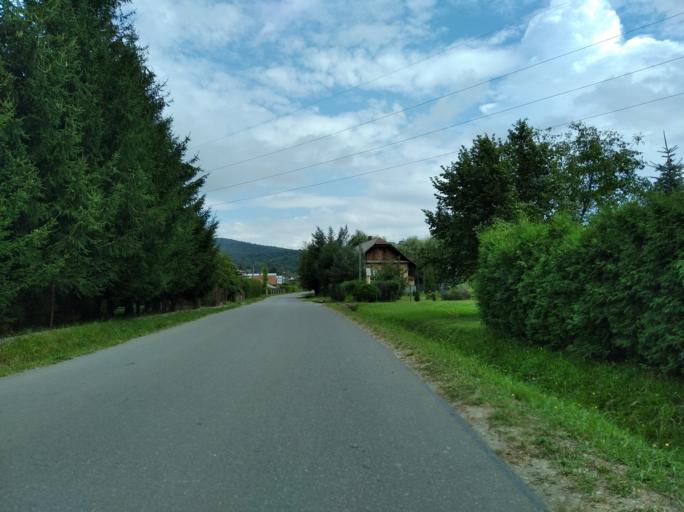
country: PL
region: Subcarpathian Voivodeship
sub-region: Powiat krosnienski
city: Odrzykon
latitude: 49.7413
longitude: 21.7499
